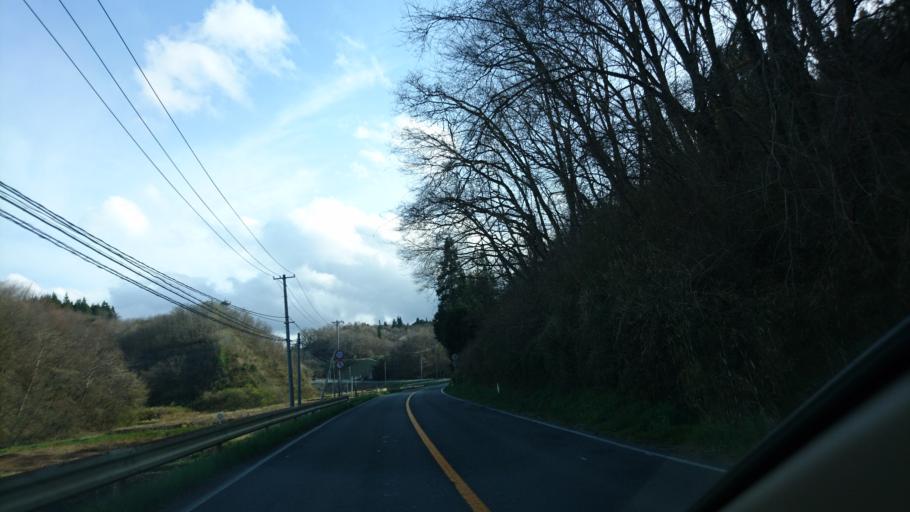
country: JP
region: Iwate
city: Ichinoseki
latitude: 38.9844
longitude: 141.3318
